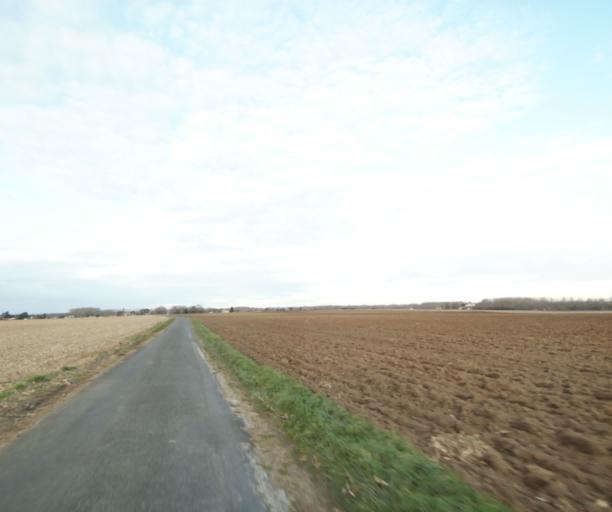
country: FR
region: Poitou-Charentes
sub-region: Departement de la Charente-Maritime
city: Les Gonds
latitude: 45.7042
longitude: -0.6145
